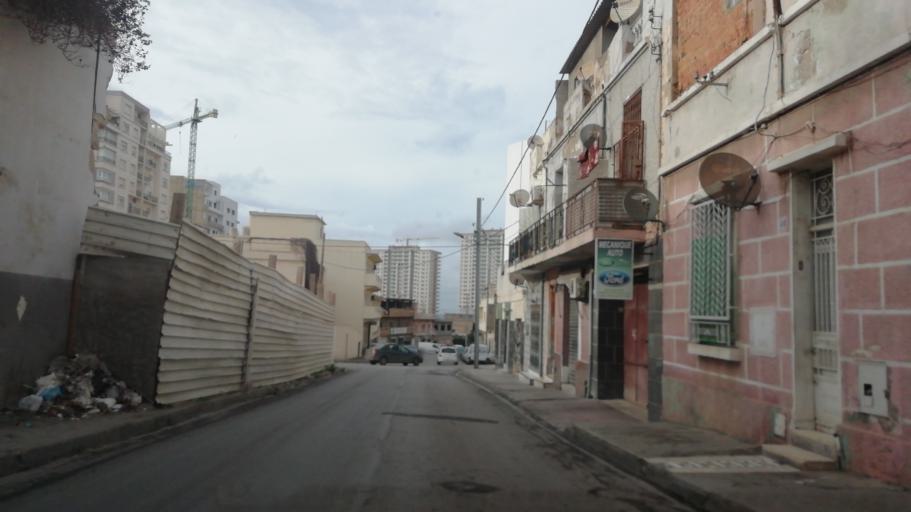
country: DZ
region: Oran
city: Oran
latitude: 35.7027
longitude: -0.6240
